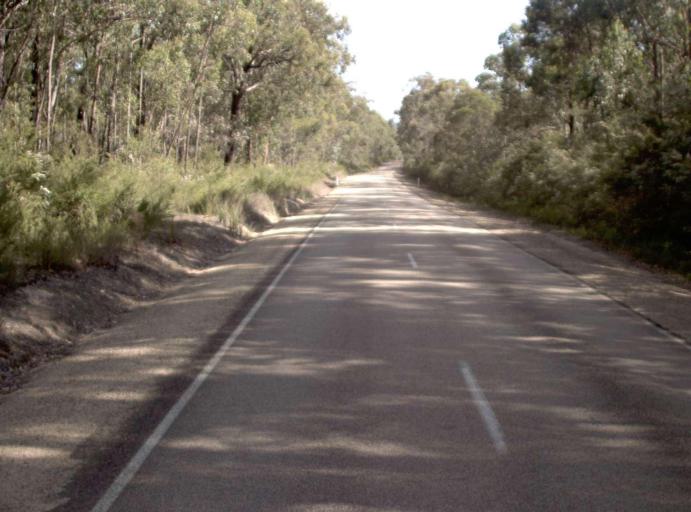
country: AU
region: Victoria
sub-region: East Gippsland
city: Lakes Entrance
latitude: -37.6366
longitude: 148.1106
